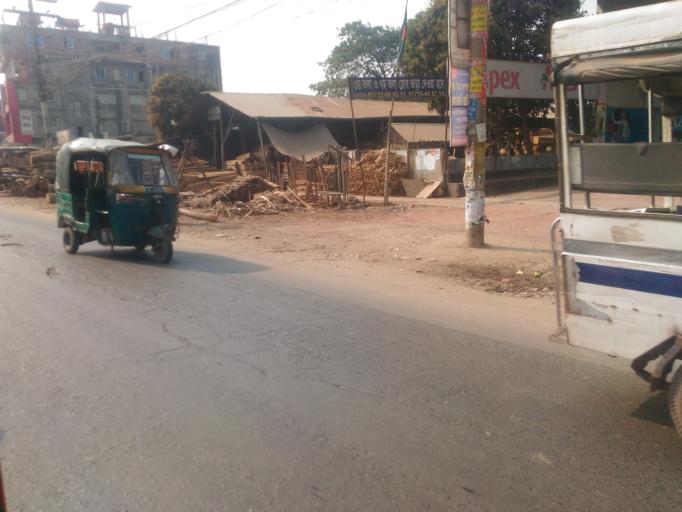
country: BD
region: Dhaka
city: Tungi
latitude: 23.9963
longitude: 90.4160
